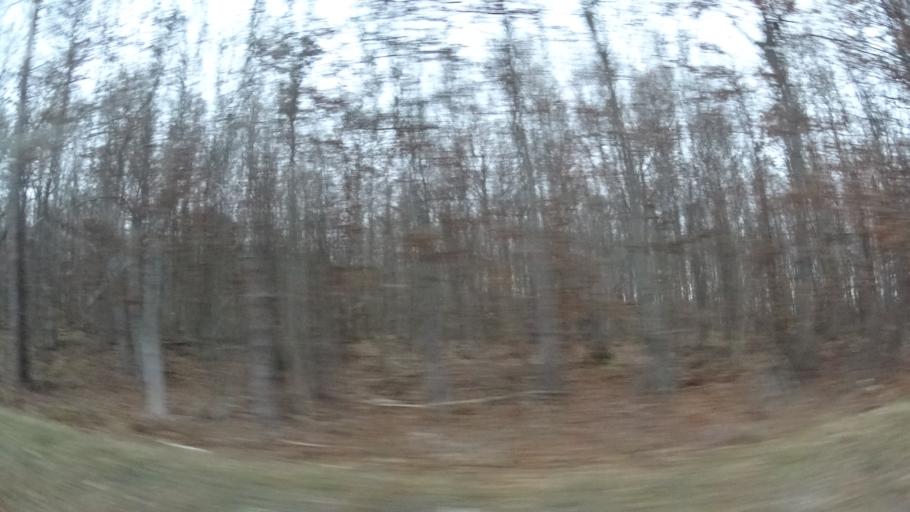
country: DE
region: Hesse
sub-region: Regierungsbezirk Kassel
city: Rasdorf
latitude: 50.7264
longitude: 9.9175
